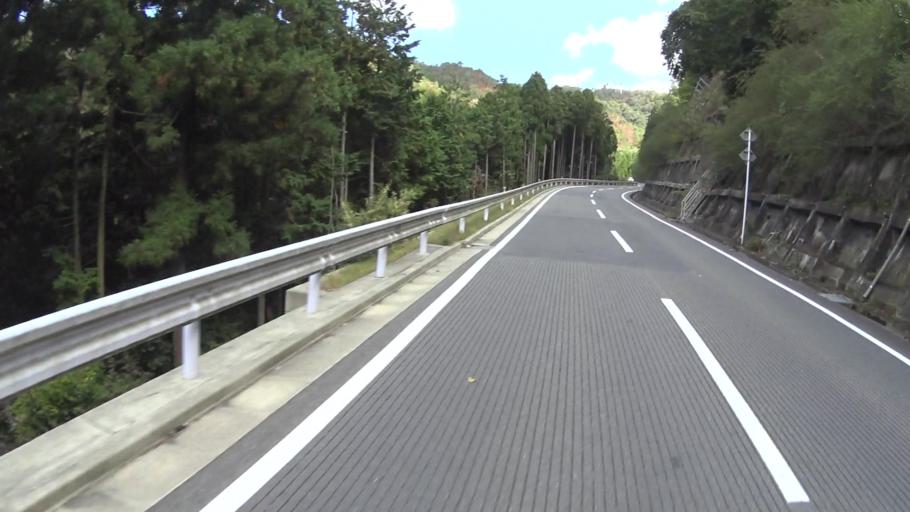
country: JP
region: Kyoto
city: Kameoka
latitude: 35.1028
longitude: 135.5528
